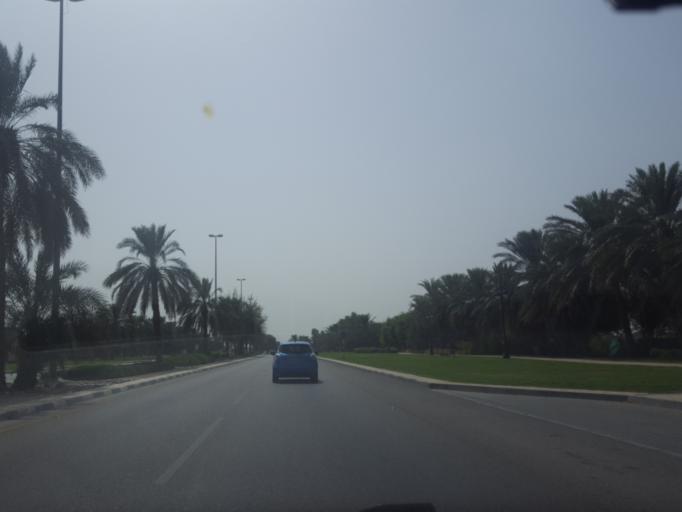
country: AE
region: Abu Dhabi
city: Al Ain
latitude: 24.2058
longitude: 55.7931
